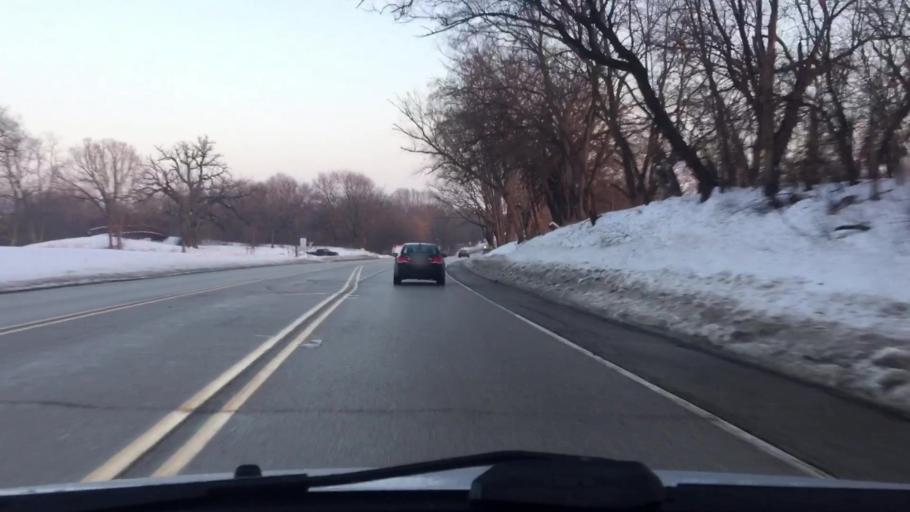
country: US
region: Illinois
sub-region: Kane County
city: Village of Campton Hills
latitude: 41.9333
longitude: -88.3834
